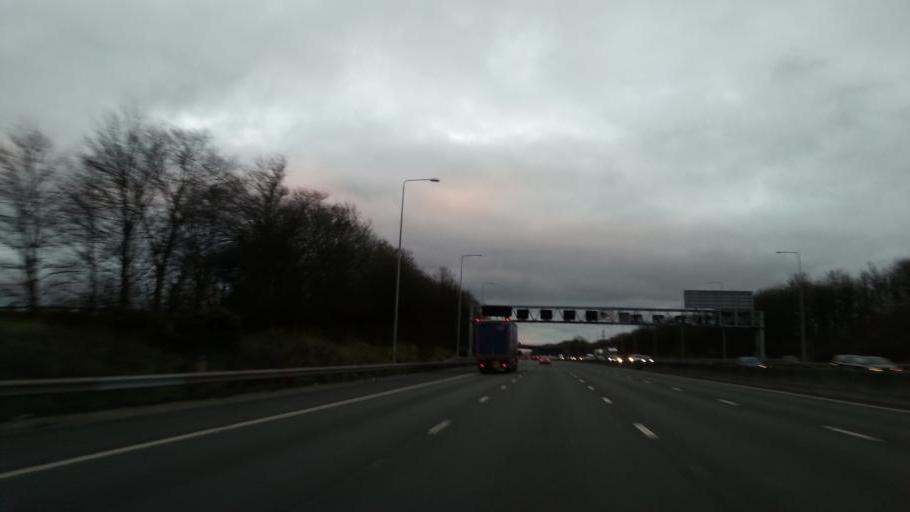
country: GB
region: England
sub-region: Derbyshire
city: Pinxton
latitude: 53.0846
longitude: -1.2995
